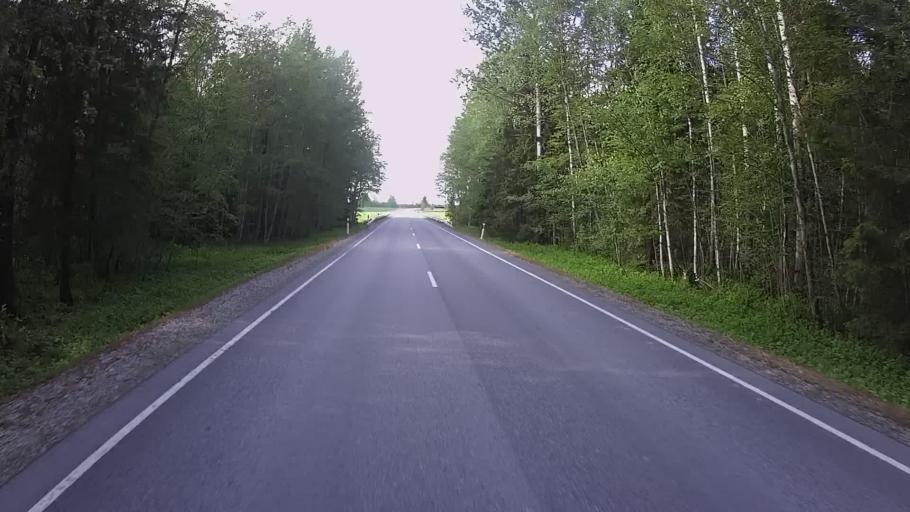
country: EE
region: Jogevamaa
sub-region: Mustvee linn
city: Mustvee
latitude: 58.8839
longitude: 26.8144
